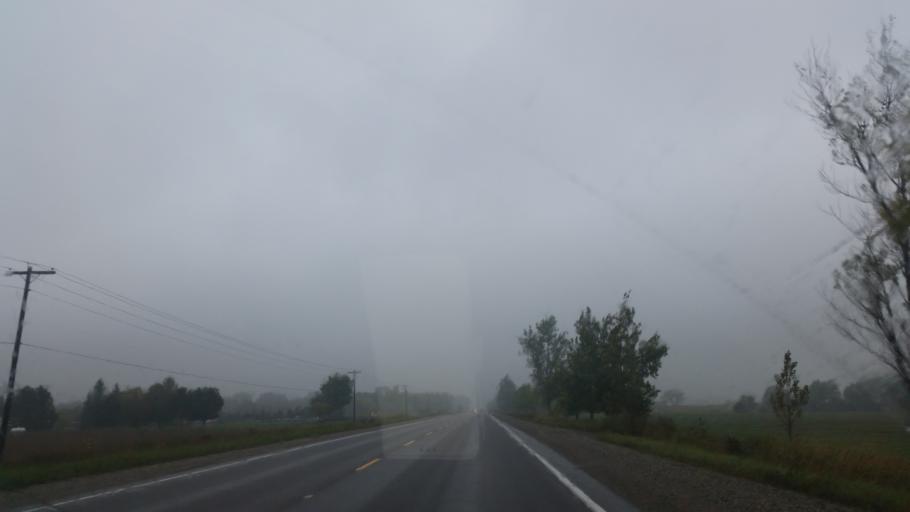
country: CA
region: Ontario
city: Stratford
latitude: 43.2909
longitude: -81.0504
